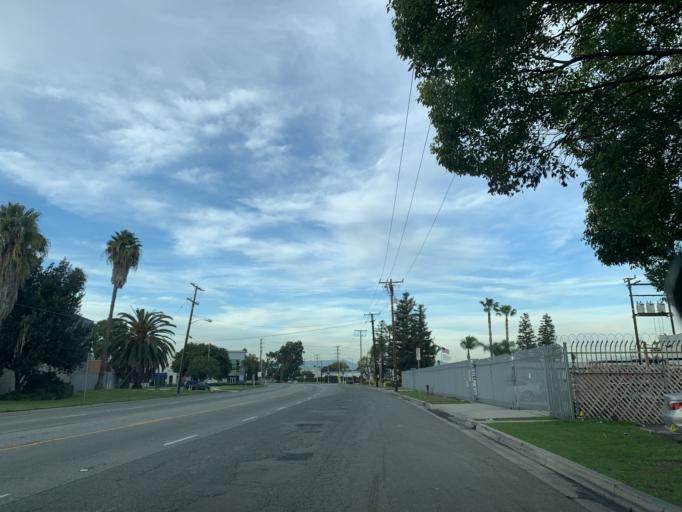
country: US
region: California
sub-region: Los Angeles County
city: Compton
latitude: 33.8630
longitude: -118.2134
